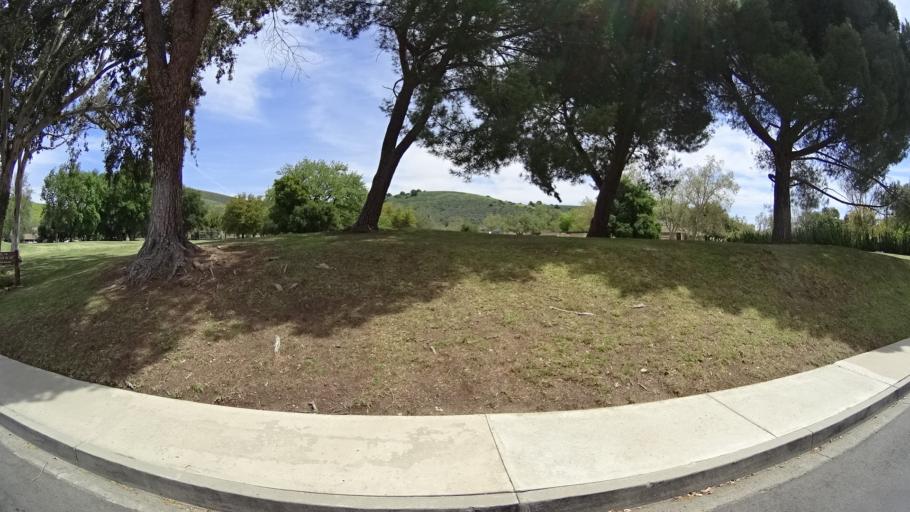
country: US
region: California
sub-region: Ventura County
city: Thousand Oaks
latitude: 34.1686
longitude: -118.8286
